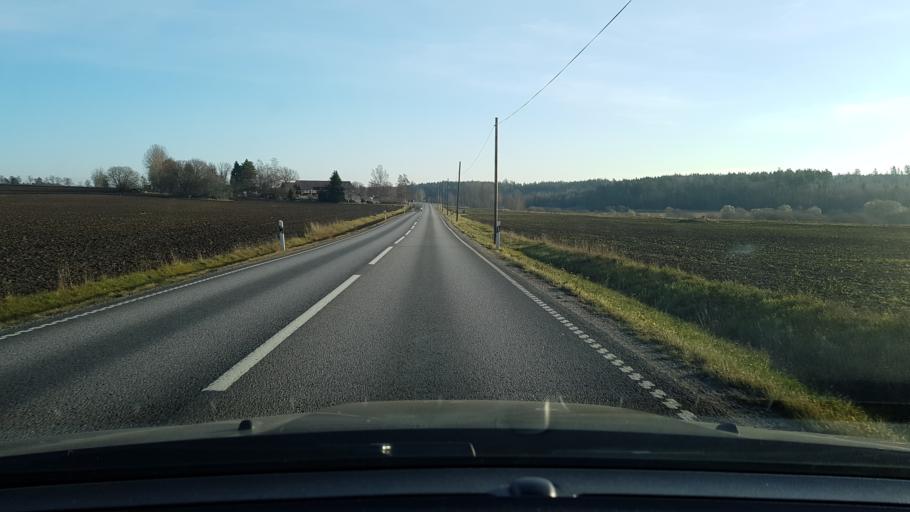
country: SE
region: Stockholm
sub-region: Norrtalje Kommun
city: Nykvarn
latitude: 59.7372
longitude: 18.2440
